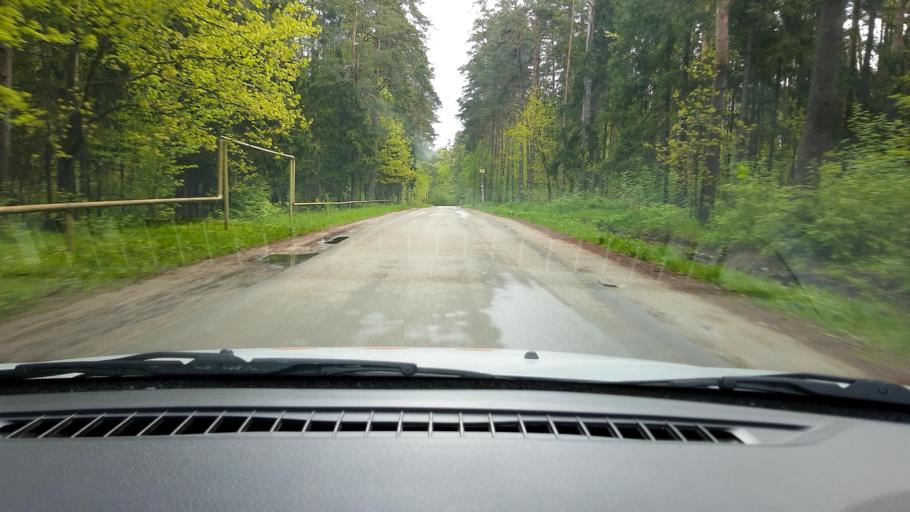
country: RU
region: Nizjnij Novgorod
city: Afonino
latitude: 56.1781
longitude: 44.0778
